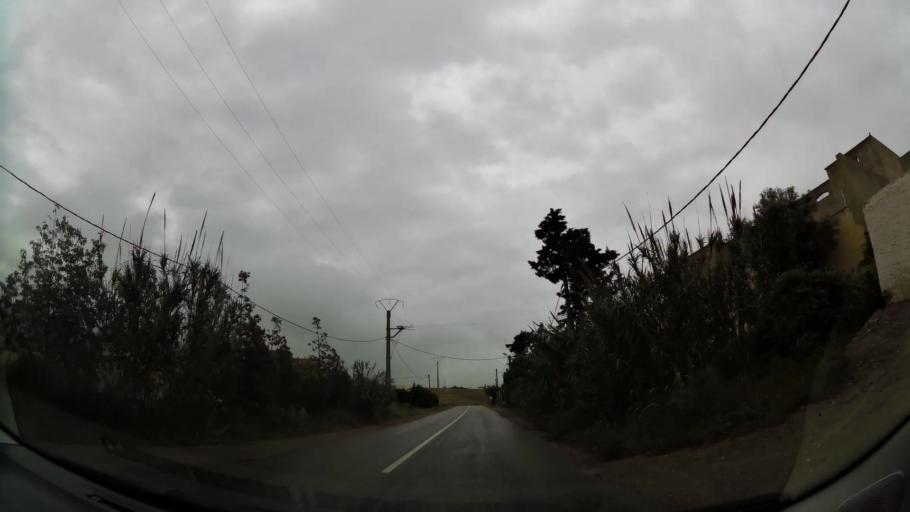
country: MA
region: Oriental
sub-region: Nador
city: Nador
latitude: 35.1416
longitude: -3.0458
